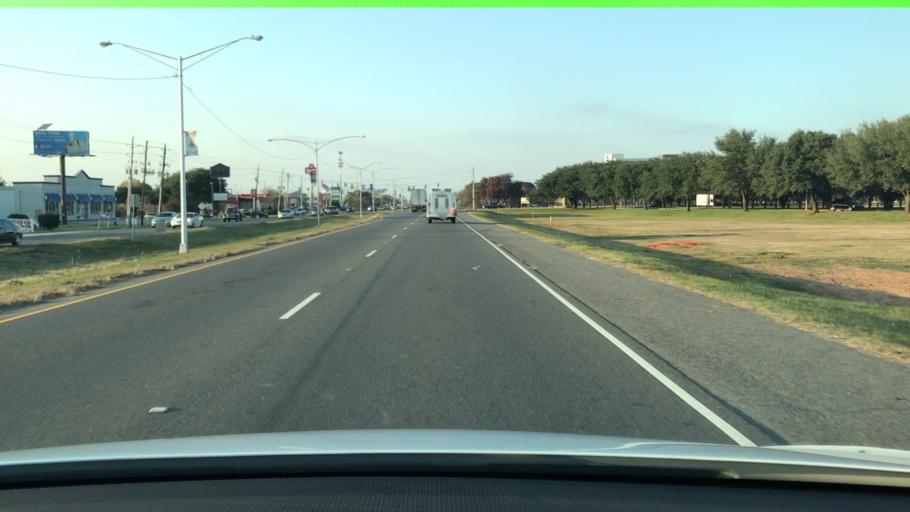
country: US
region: Louisiana
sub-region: Bossier Parish
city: Bossier City
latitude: 32.4250
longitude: -93.7078
